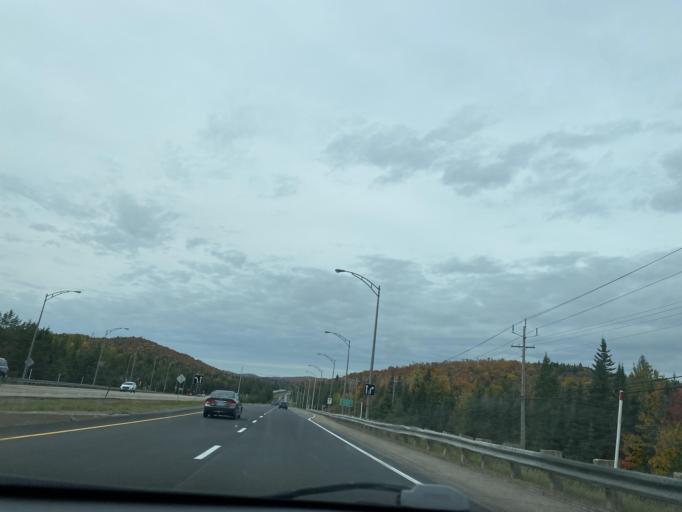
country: CA
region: Quebec
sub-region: Laurentides
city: Sainte-Agathe-des-Monts
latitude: 46.0891
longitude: -74.3283
